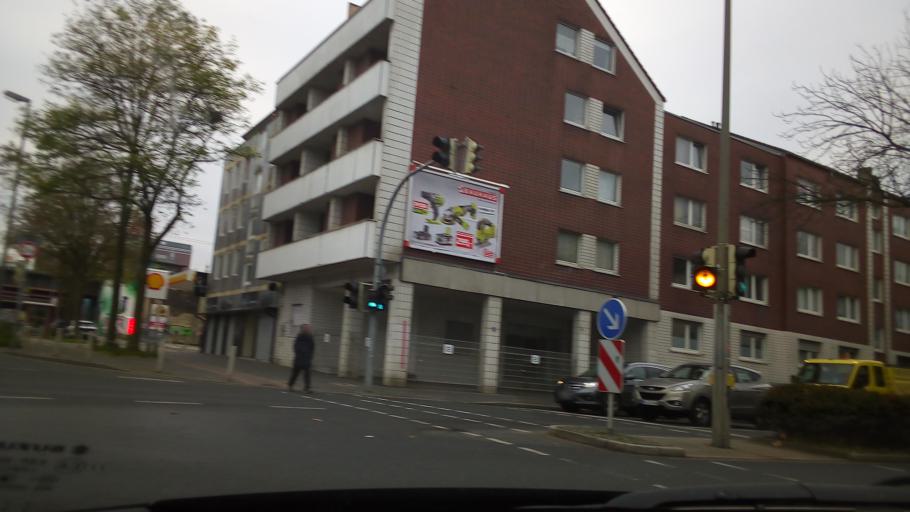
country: DE
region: North Rhine-Westphalia
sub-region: Regierungsbezirk Arnsberg
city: Dortmund
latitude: 51.5195
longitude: 7.4533
